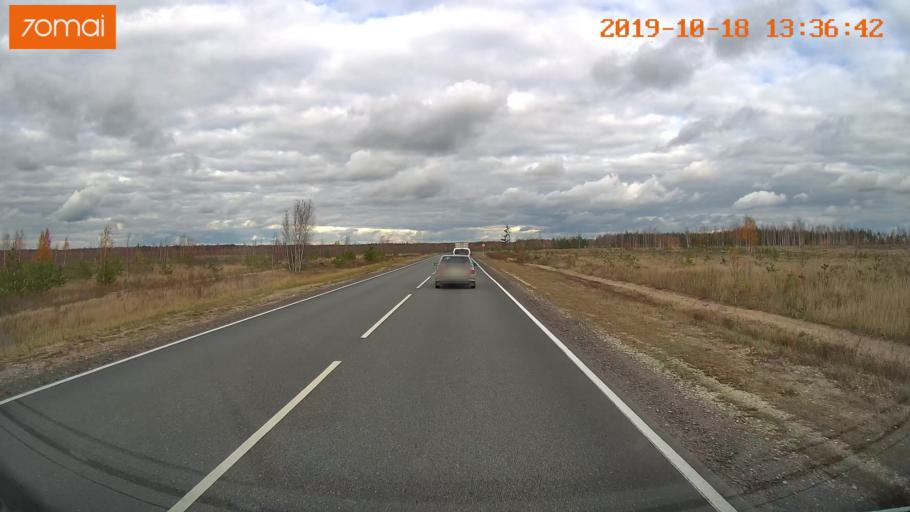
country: RU
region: Rjazan
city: Solotcha
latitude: 54.8730
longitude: 39.9866
